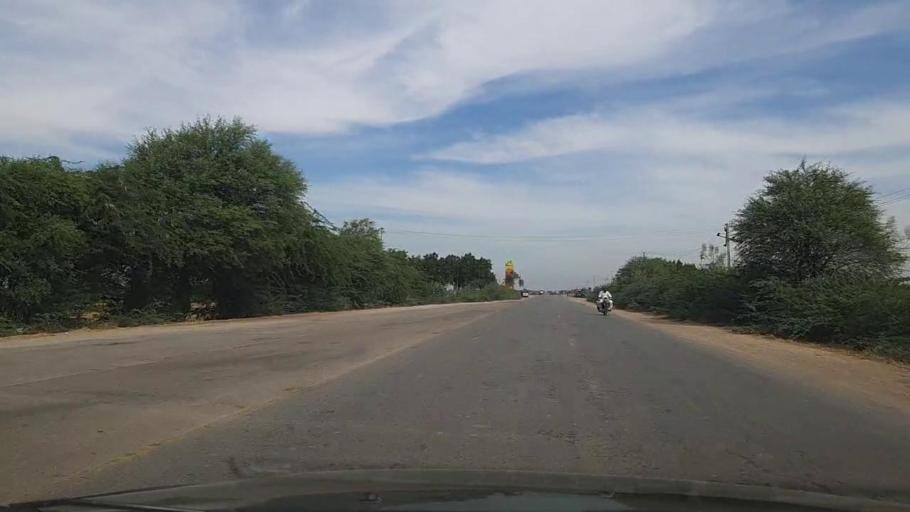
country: PK
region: Sindh
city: Thatta
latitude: 24.7676
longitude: 67.9380
